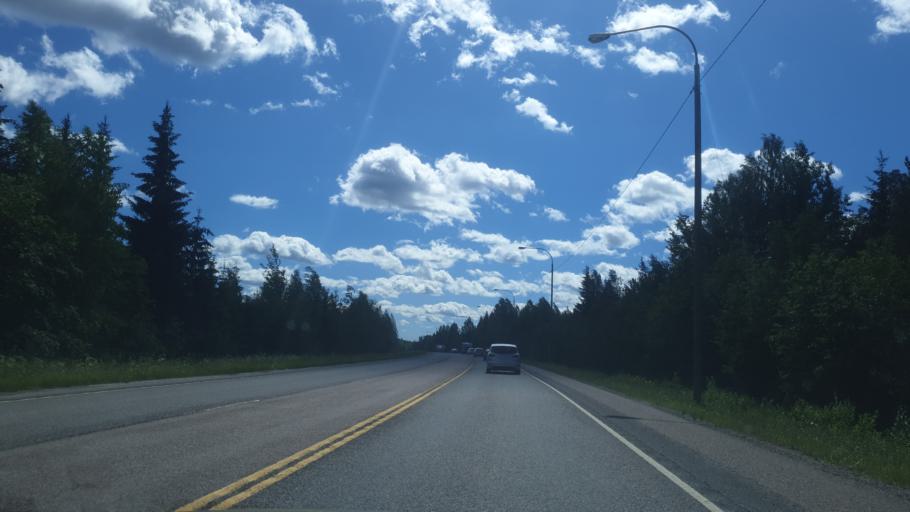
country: FI
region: Northern Savo
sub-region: Varkaus
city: Varkaus
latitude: 62.3611
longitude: 27.8102
